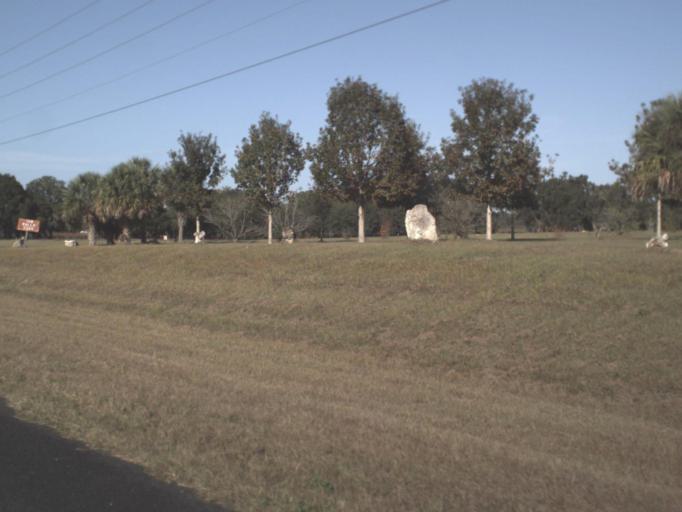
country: US
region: Florida
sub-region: Marion County
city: Belleview
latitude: 29.0260
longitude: -82.1087
